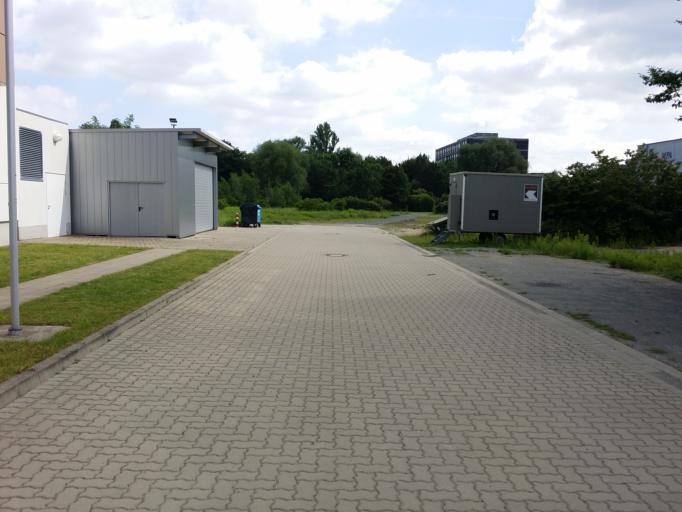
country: DE
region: Lower Saxony
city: Braunschweig
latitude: 52.2828
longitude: 10.5484
